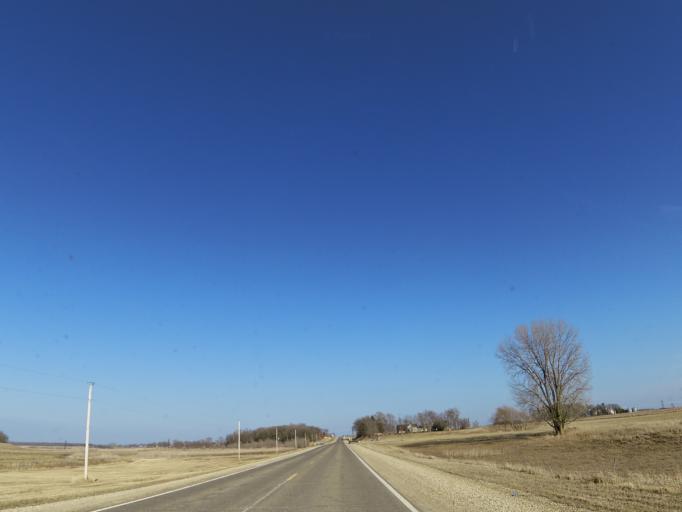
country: US
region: Iowa
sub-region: Worth County
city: Northwood
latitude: 43.4443
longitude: -93.3043
